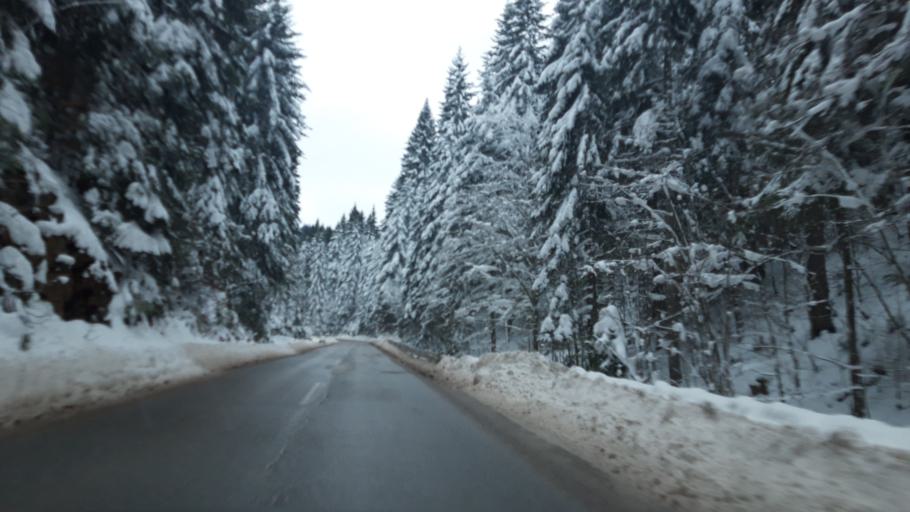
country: BA
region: Republika Srpska
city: Koran
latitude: 43.7556
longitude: 18.5490
